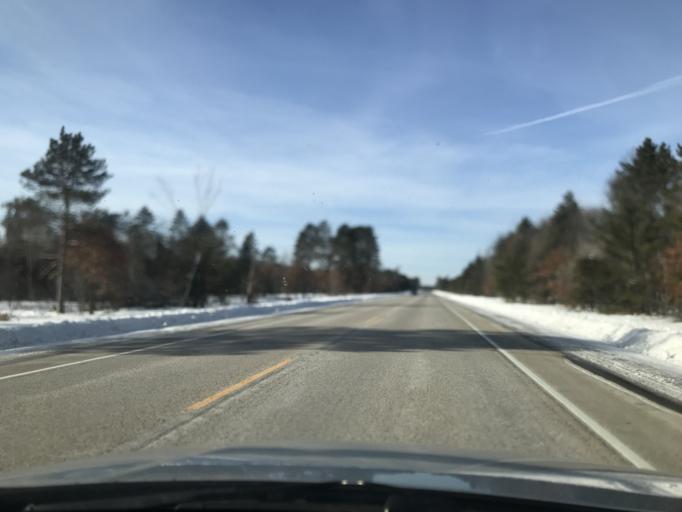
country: US
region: Wisconsin
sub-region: Oconto County
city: Gillett
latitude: 45.1182
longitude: -88.3846
